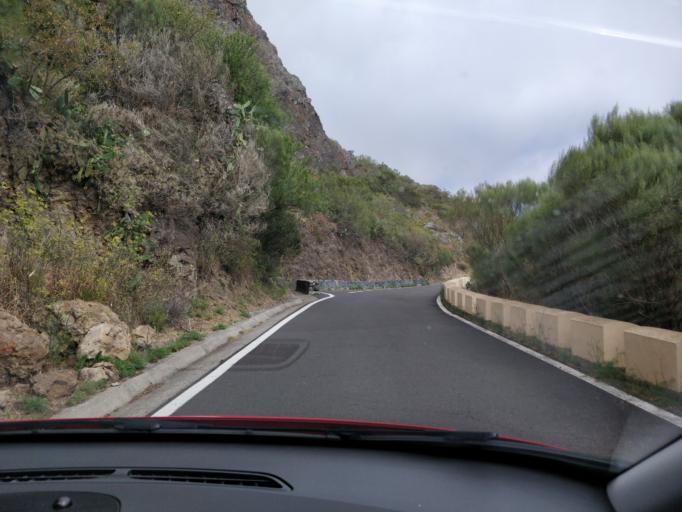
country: ES
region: Canary Islands
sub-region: Provincia de Santa Cruz de Tenerife
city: Santiago del Teide
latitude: 28.3186
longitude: -16.8534
